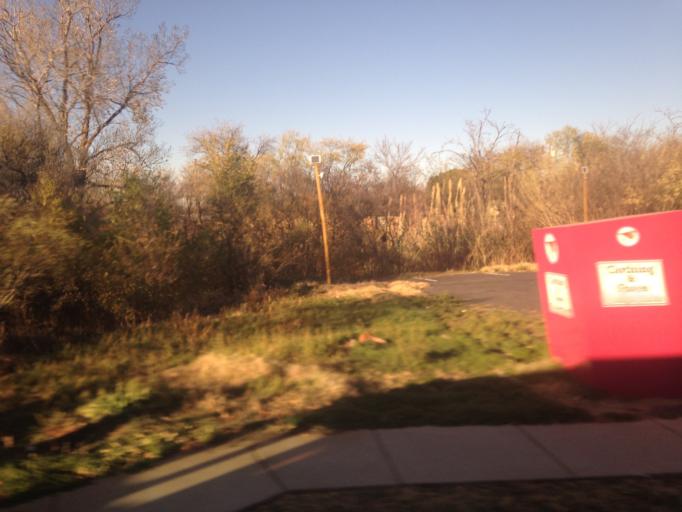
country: US
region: Texas
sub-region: Taylor County
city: Abilene
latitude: 32.4438
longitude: -99.7692
